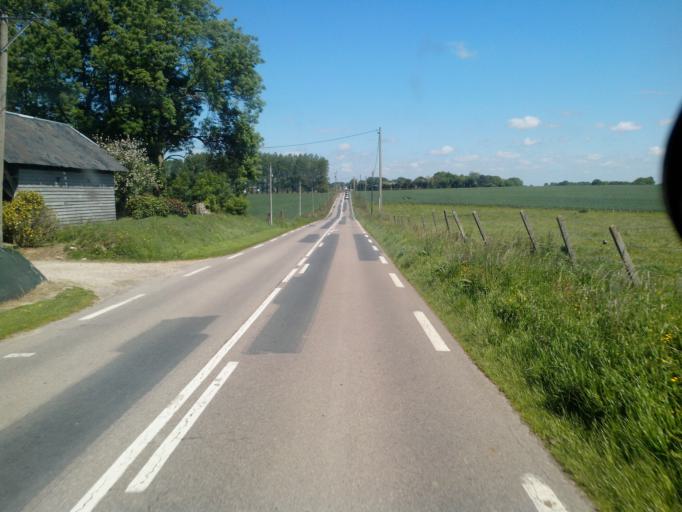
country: FR
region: Haute-Normandie
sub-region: Departement de la Seine-Maritime
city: Gonneville-la-Mallet
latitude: 49.6417
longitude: 0.2457
